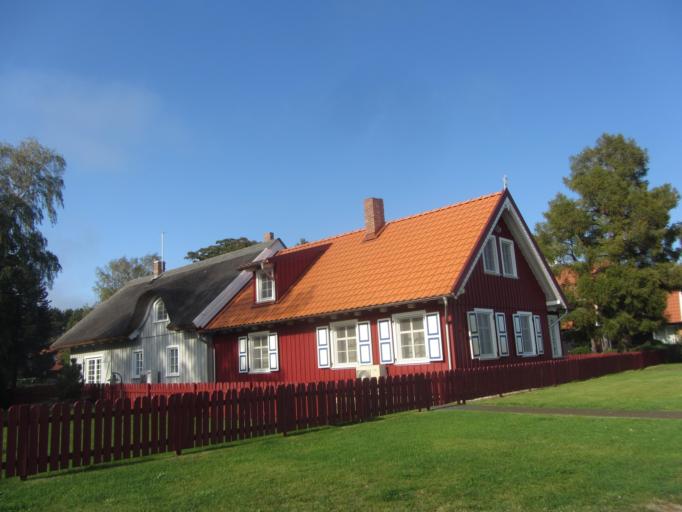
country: LT
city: Neringa
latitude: 55.4132
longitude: 21.0959
